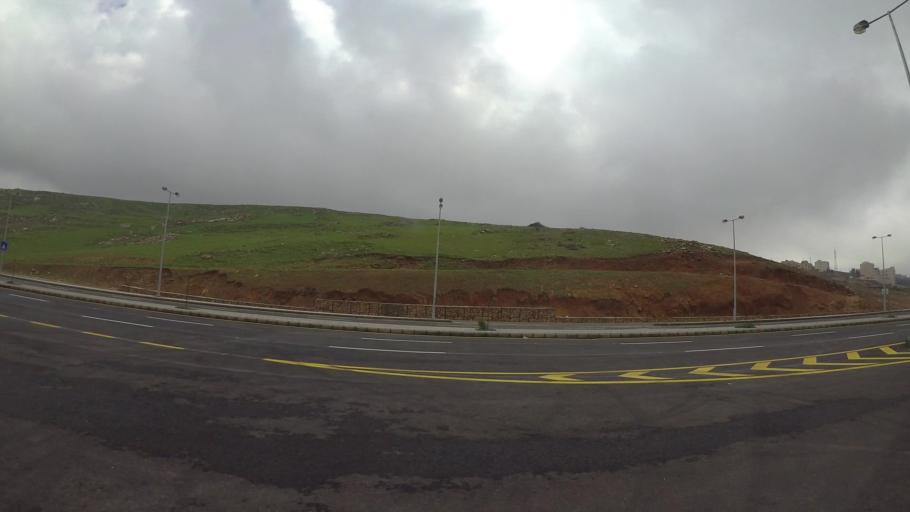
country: JO
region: Amman
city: Al Bunayyat ash Shamaliyah
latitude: 31.9344
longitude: 35.8674
